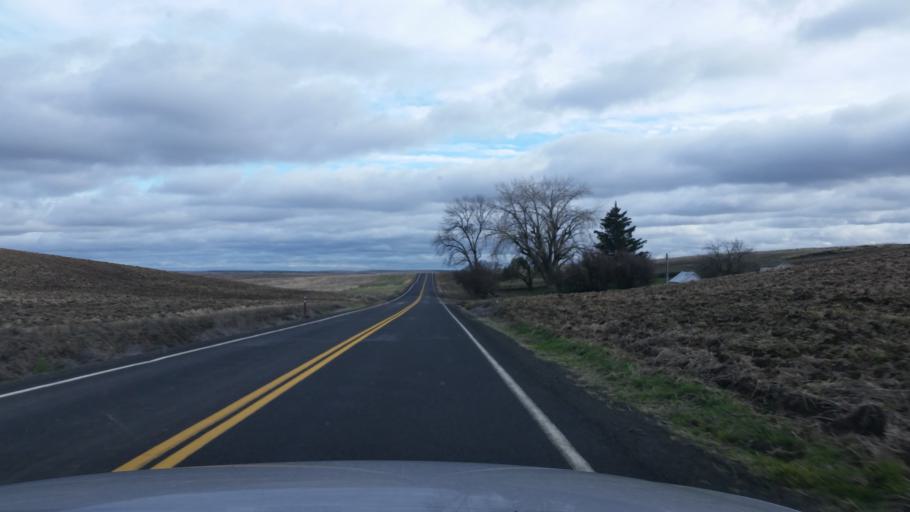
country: US
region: Washington
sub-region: Lincoln County
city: Davenport
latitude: 47.3451
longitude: -118.0174
